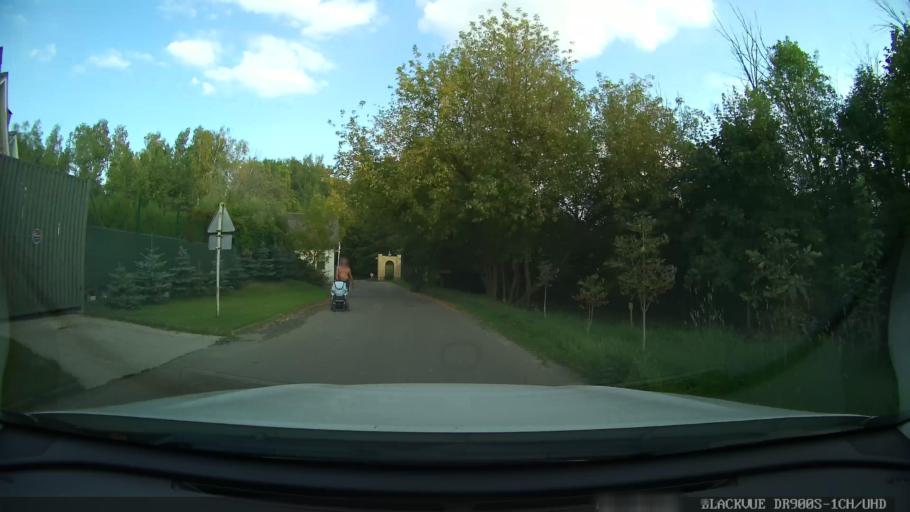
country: RU
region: Moskovskaya
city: Nemchinovka
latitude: 55.7388
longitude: 37.3423
